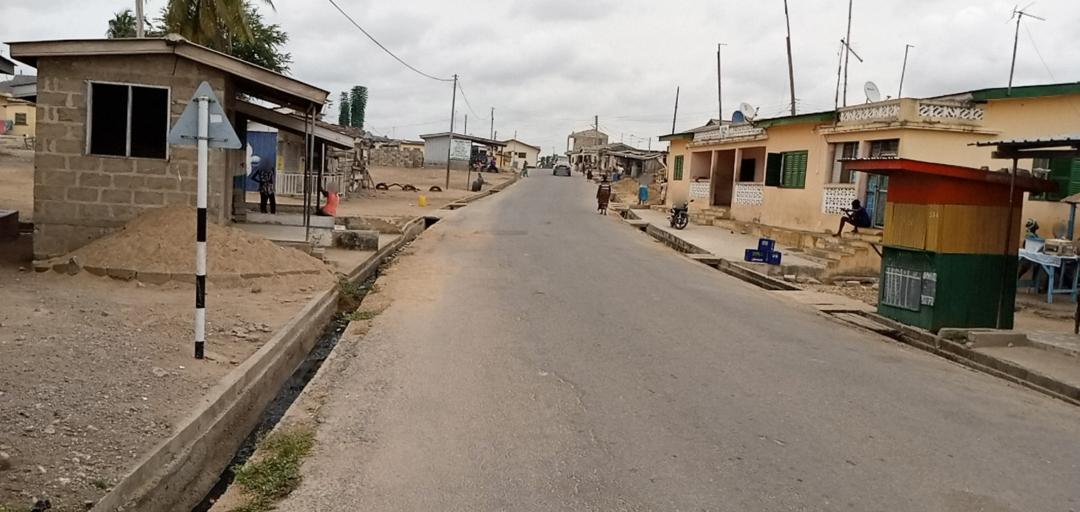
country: GH
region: Central
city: Winneba
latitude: 5.3485
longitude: -0.6212
